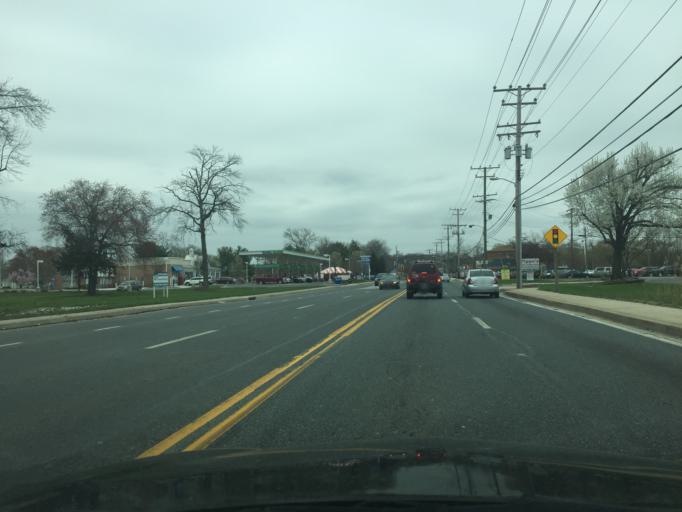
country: US
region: Maryland
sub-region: Baltimore County
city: Bowleys Quarters
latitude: 39.3370
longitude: -76.4071
